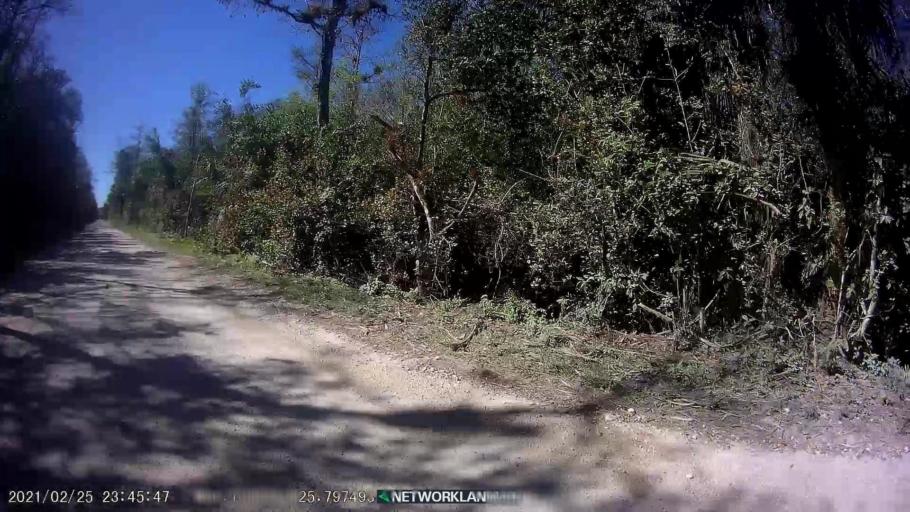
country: US
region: Florida
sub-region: Collier County
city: Marco
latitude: 25.7973
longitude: -81.1006
